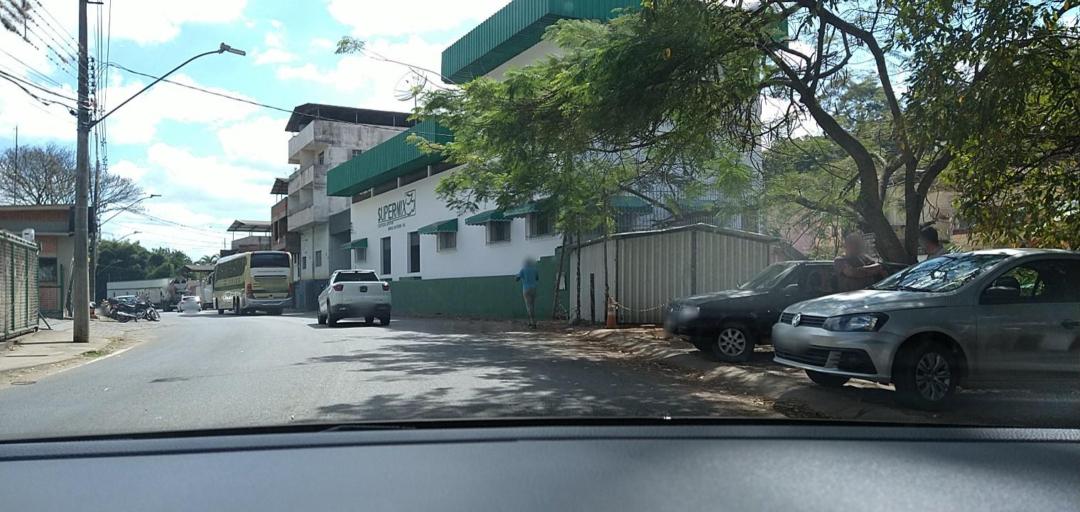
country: BR
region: Minas Gerais
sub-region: Ponte Nova
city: Ponte Nova
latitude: -20.4209
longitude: -42.8986
